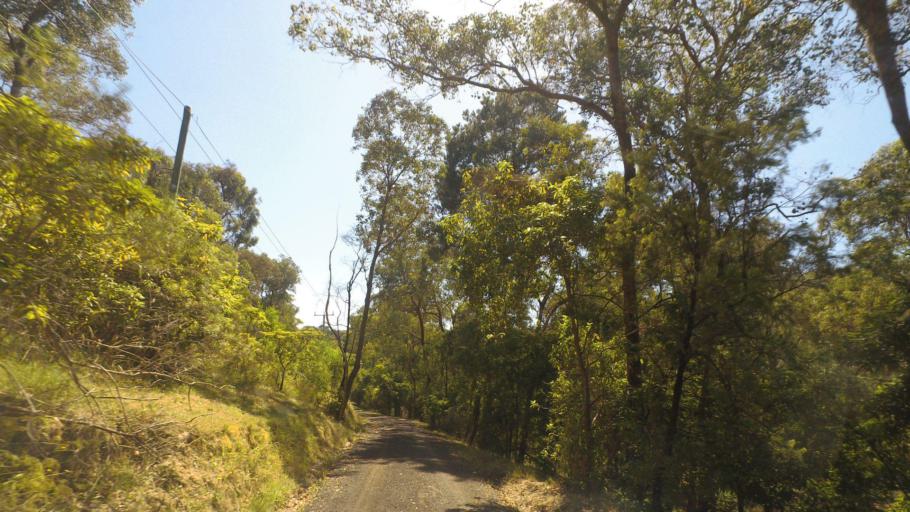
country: AU
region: Victoria
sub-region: Manningham
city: Park Orchards
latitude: -37.7754
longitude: 145.2096
